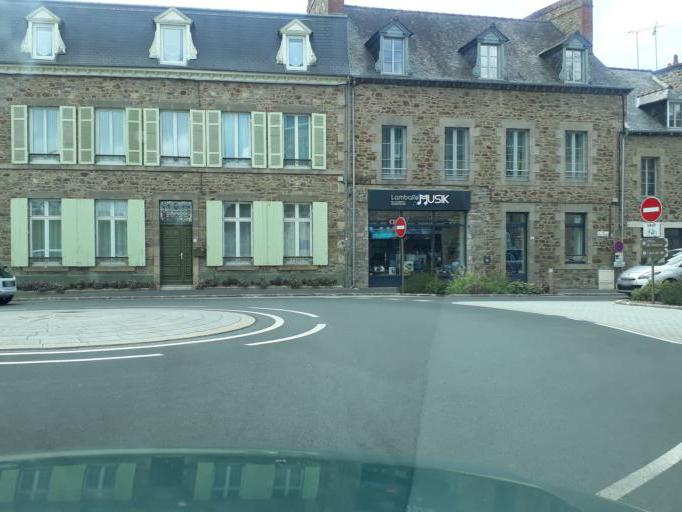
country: FR
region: Brittany
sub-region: Departement des Cotes-d'Armor
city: Lamballe
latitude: 48.4664
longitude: -2.5135
